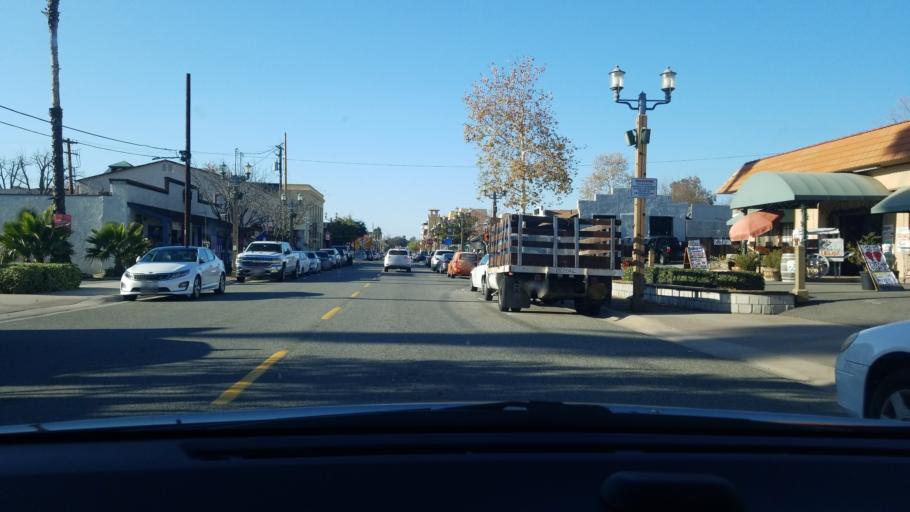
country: US
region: California
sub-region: Riverside County
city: Temecula
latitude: 33.4929
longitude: -117.1481
